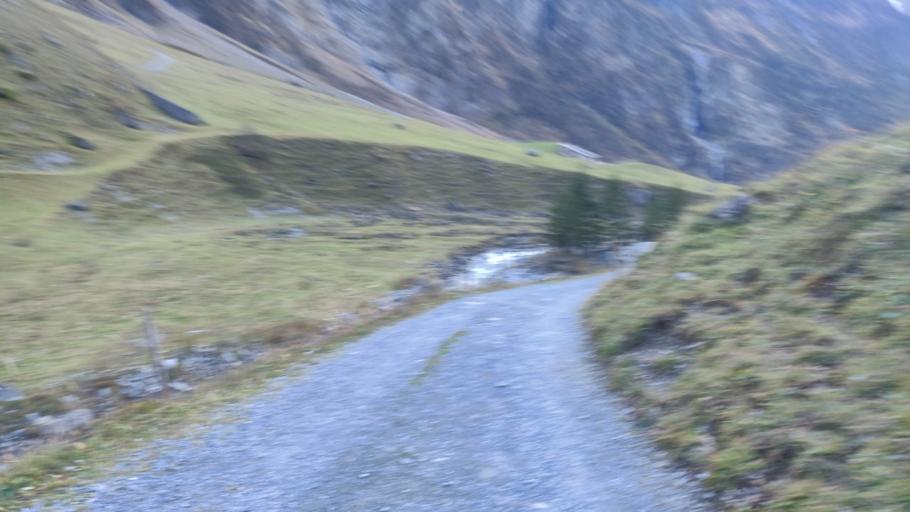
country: CH
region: Obwalden
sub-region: Obwalden
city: Engelberg
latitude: 46.8034
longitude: 8.4980
